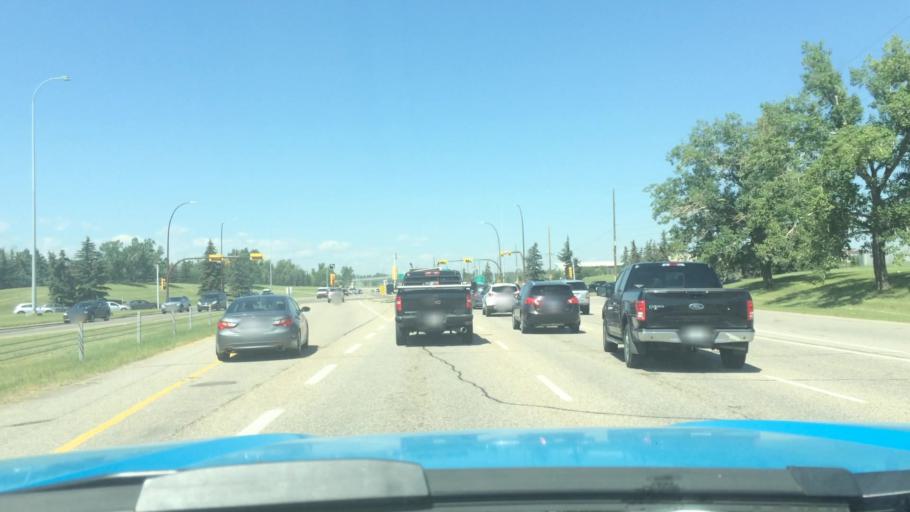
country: CA
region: Alberta
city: Calgary
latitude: 50.9490
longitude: -114.0582
